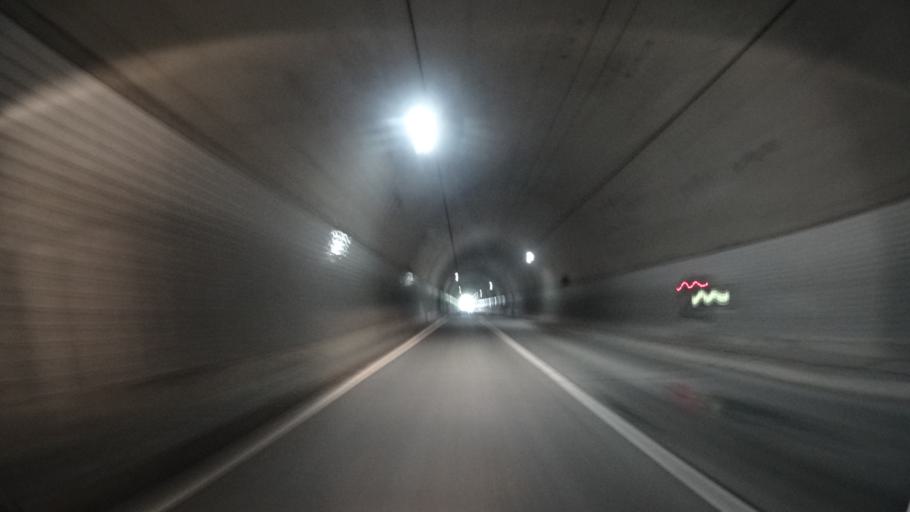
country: JP
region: Ehime
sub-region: Nishiuwa-gun
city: Ikata-cho
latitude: 33.3928
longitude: 132.1366
